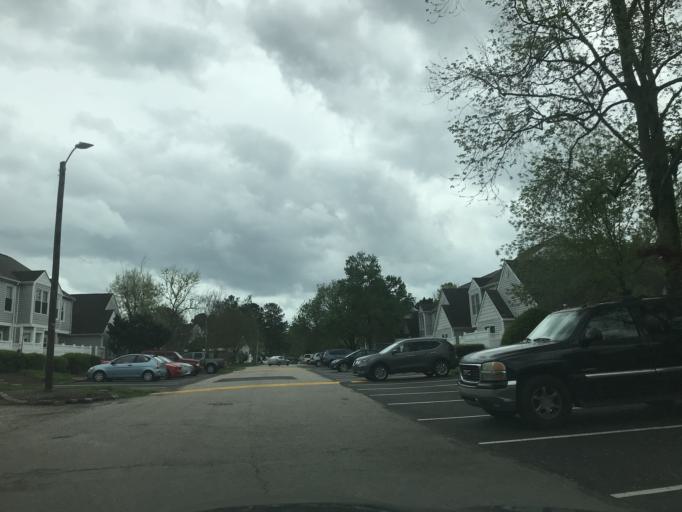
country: US
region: North Carolina
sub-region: Wake County
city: Raleigh
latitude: 35.8549
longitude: -78.5783
